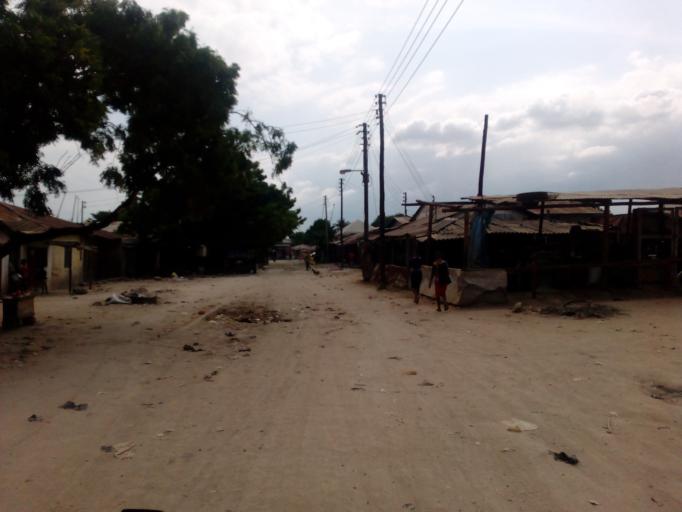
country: TZ
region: Dar es Salaam
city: Dar es Salaam
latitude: -6.8548
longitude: 39.2578
